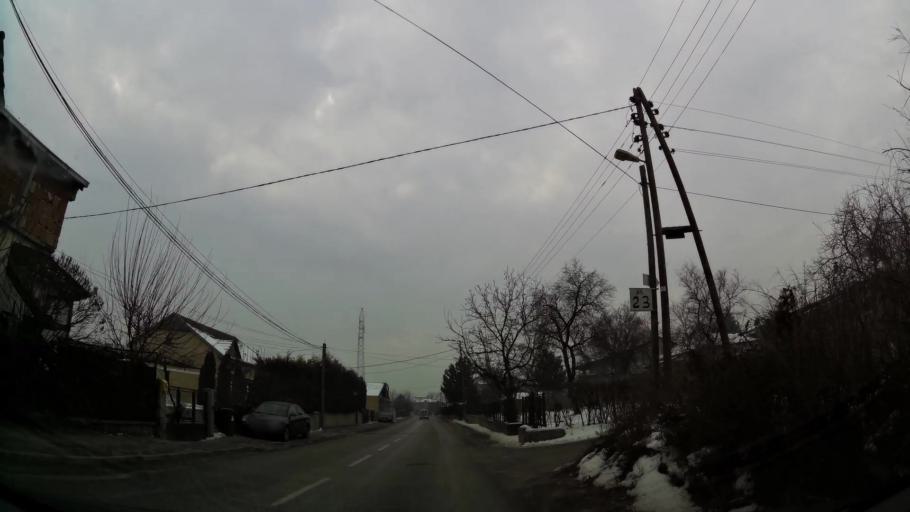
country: MK
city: Kondovo
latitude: 42.0416
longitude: 21.3472
